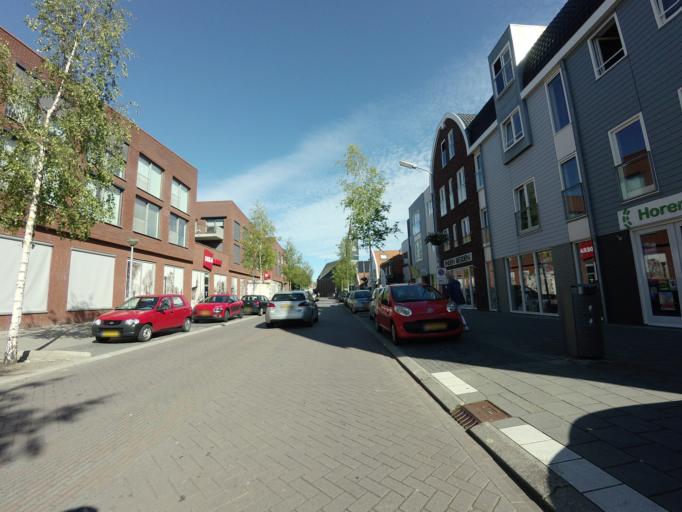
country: NL
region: North Holland
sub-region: Gemeente Uitgeest
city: Uitgeest
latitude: 52.5005
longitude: 4.7670
